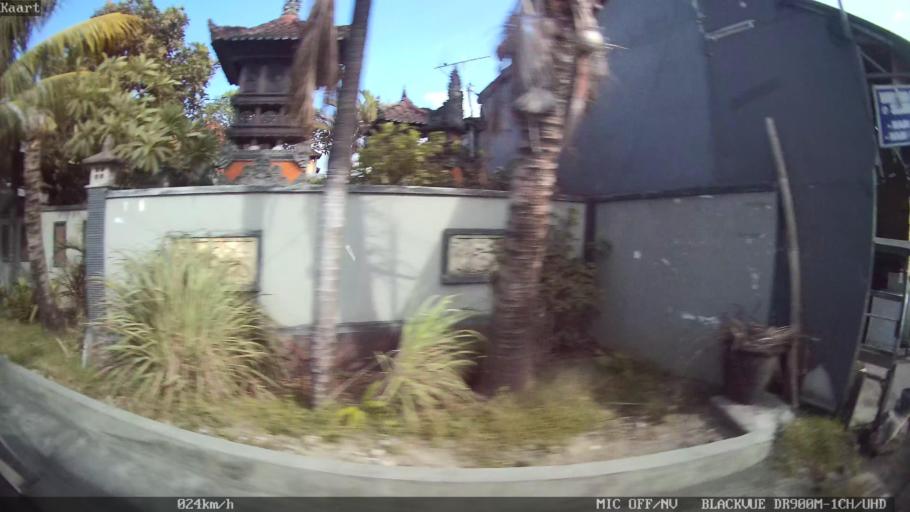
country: ID
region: Bali
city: Jabajero
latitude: -8.7182
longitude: 115.1881
